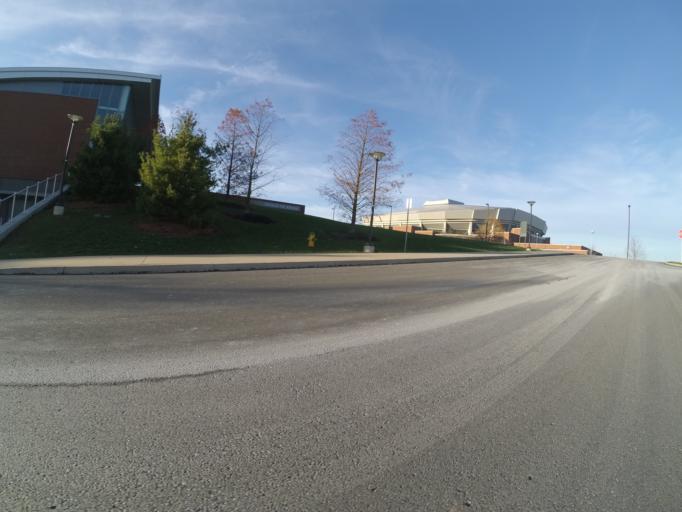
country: US
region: Pennsylvania
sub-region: Centre County
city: State College
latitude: 40.8068
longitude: -77.8557
